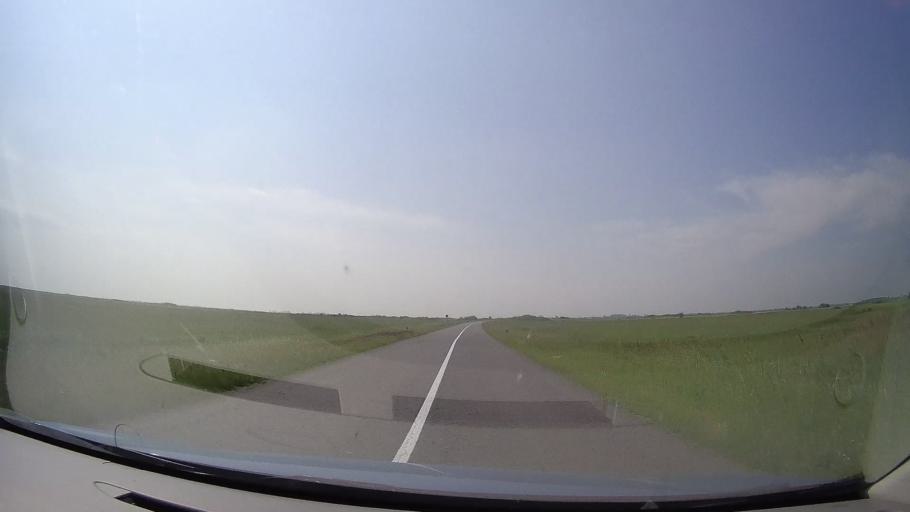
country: RS
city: Jarkovac
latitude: 45.3000
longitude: 20.7623
